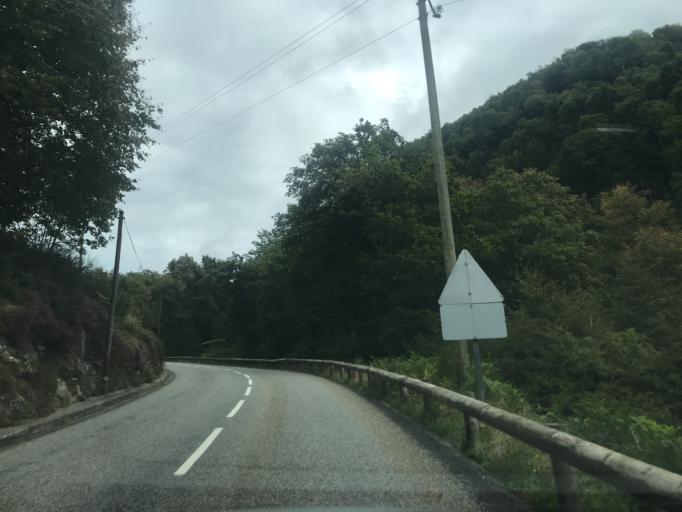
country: FR
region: Midi-Pyrenees
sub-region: Departement de la Haute-Garonne
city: Bagneres-de-Luchon
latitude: 42.7701
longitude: 0.6237
